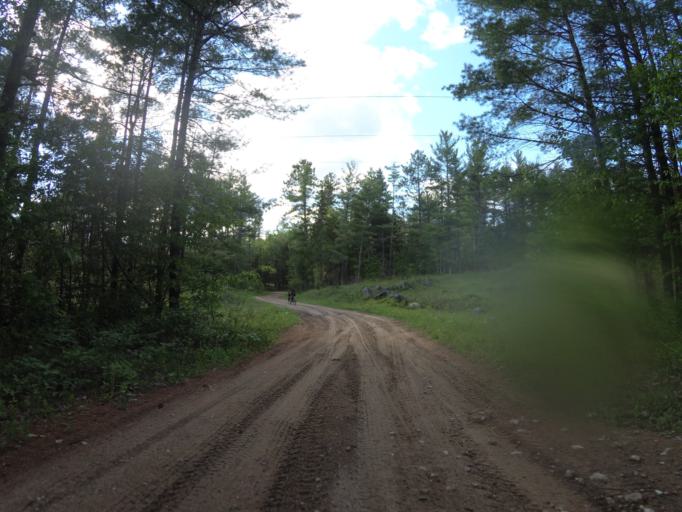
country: CA
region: Ontario
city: Renfrew
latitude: 45.1614
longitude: -76.9523
